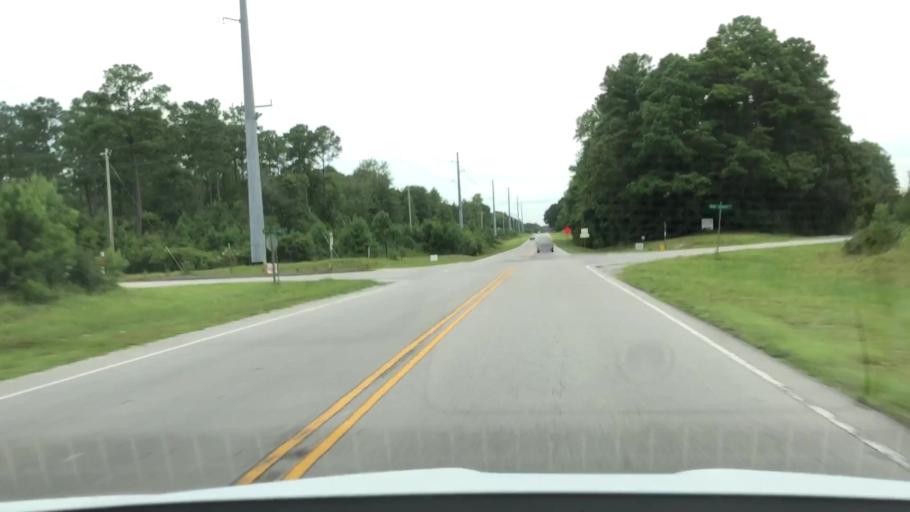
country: US
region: North Carolina
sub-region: Carteret County
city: Cape Carteret
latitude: 34.7506
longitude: -77.0925
